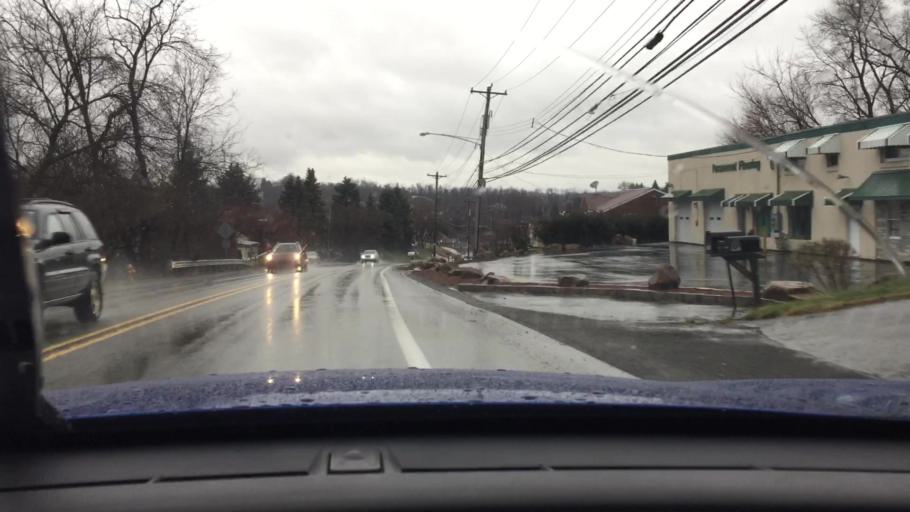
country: US
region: Pennsylvania
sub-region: Allegheny County
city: Wilson
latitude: 40.3106
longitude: -79.9158
